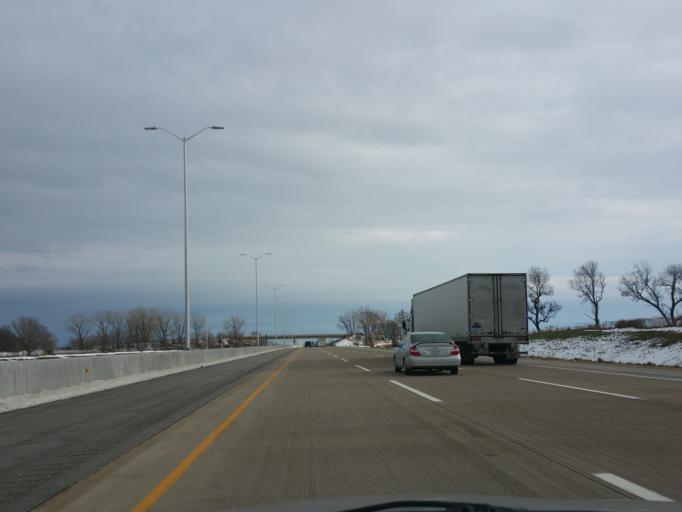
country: US
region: Illinois
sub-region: Boone County
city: Belvidere
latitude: 42.2272
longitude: -88.7691
